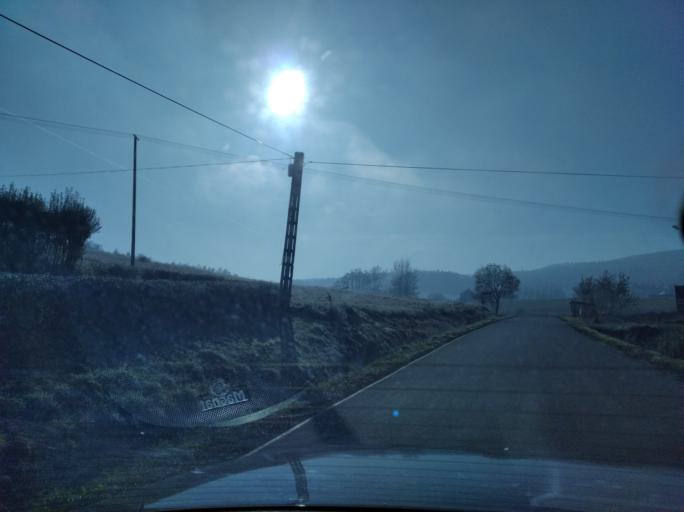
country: PL
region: Subcarpathian Voivodeship
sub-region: Powiat strzyzowski
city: Wysoka Strzyzowska
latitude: 49.8492
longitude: 21.7009
